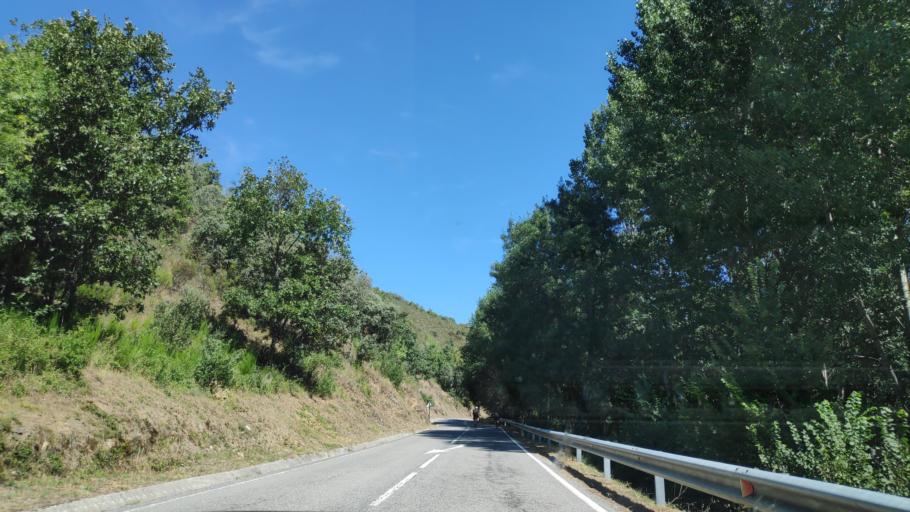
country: PT
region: Braganca
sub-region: Braganca Municipality
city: Braganca
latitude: 41.8899
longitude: -6.7303
